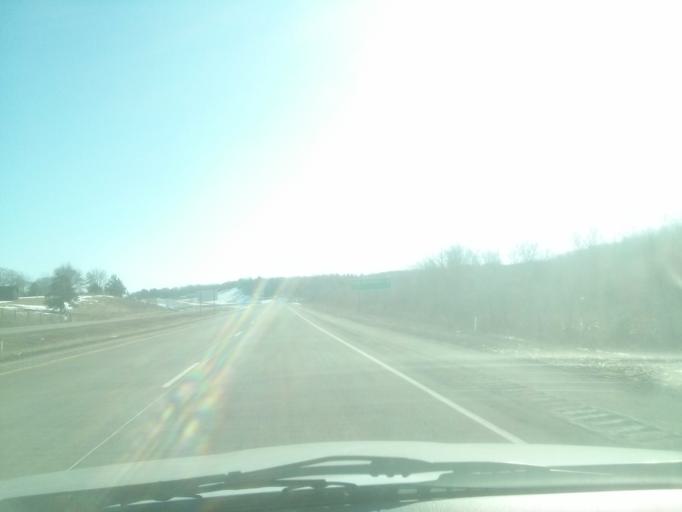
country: US
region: Wisconsin
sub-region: Saint Croix County
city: Somerset
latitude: 45.1238
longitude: -92.6410
